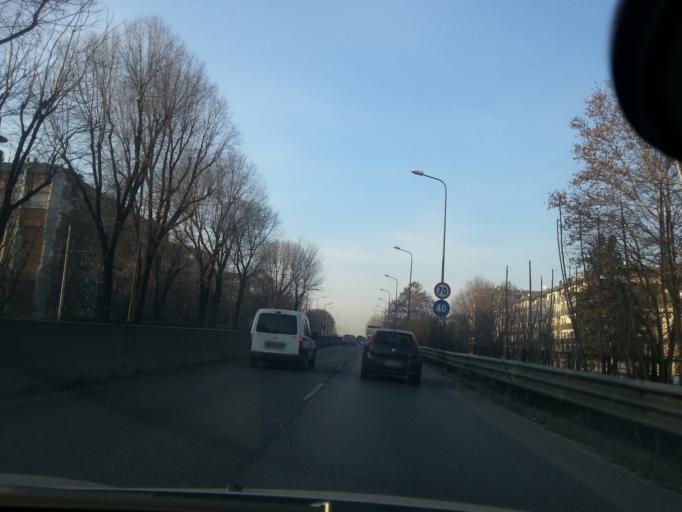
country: IT
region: Lombardy
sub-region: Citta metropolitana di Milano
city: Cormano
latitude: 45.5235
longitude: 9.1718
